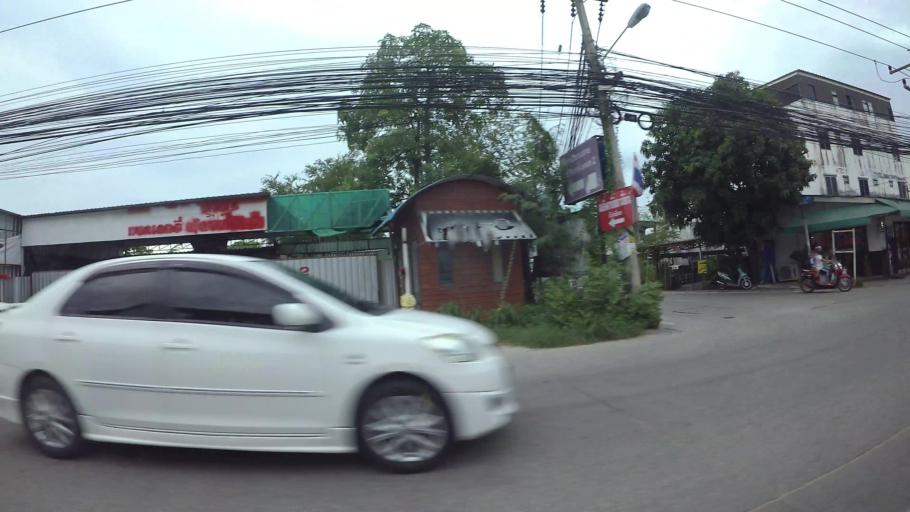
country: TH
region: Chon Buri
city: Si Racha
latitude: 13.1482
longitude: 100.9491
